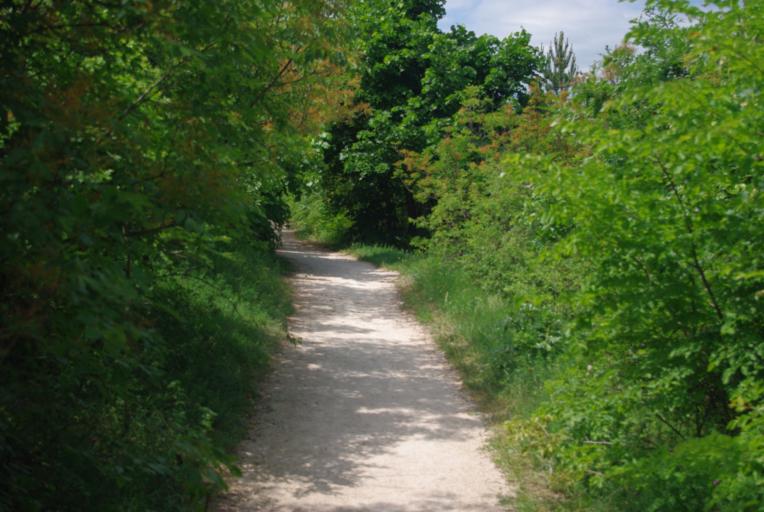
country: HU
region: Pest
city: Pilisszentivan
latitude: 47.5923
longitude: 18.8761
